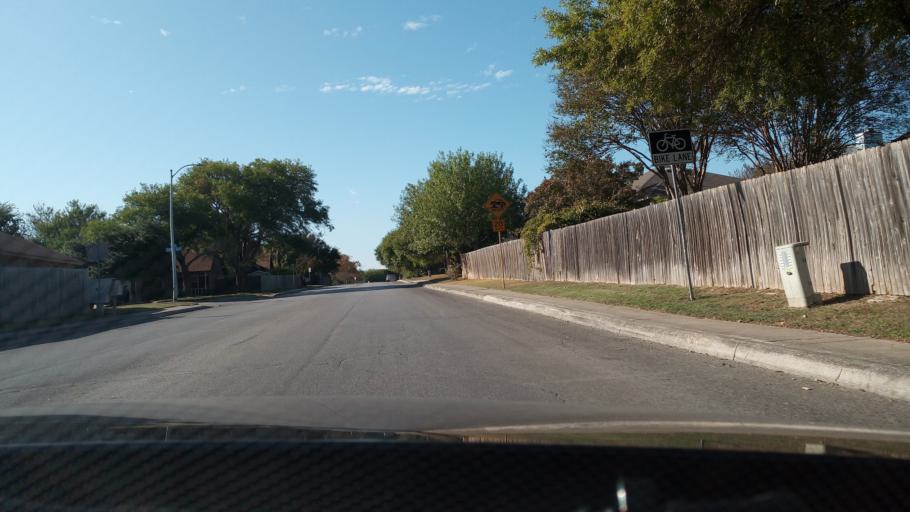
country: US
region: Texas
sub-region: Bexar County
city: Windcrest
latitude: 29.5568
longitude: -98.4341
